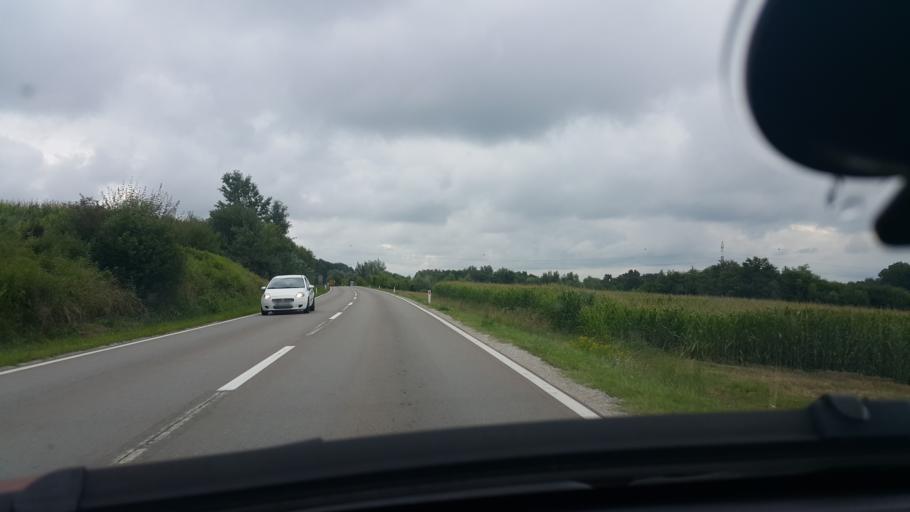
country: SI
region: Ormoz
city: Ormoz
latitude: 46.4096
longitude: 16.1242
